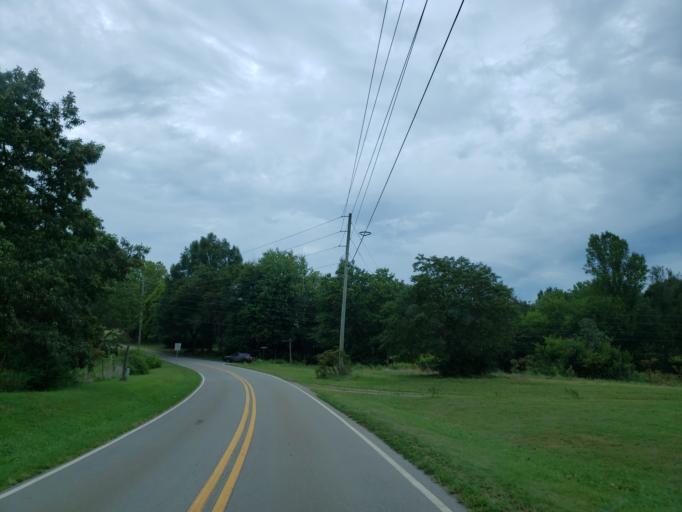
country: US
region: Georgia
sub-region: Pickens County
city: Jasper
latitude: 34.4291
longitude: -84.5522
